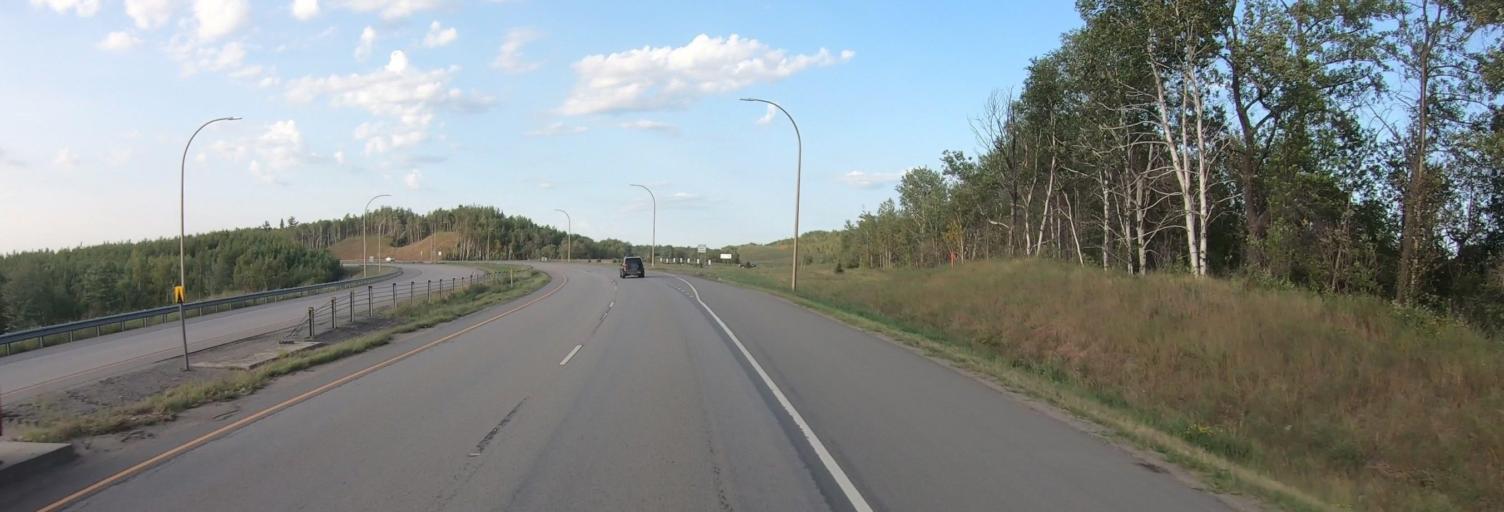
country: US
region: Minnesota
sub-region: Saint Louis County
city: Virginia
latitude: 47.5086
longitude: -92.5128
